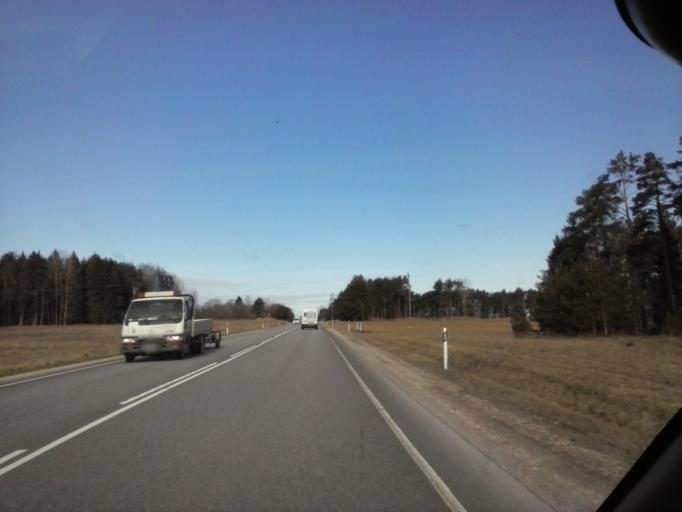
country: EE
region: Harju
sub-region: Anija vald
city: Kehra
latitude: 59.0964
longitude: 25.3811
